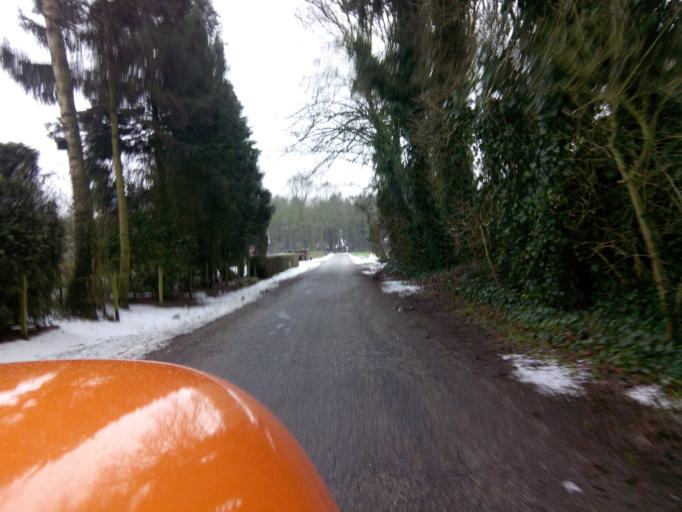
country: NL
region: Gelderland
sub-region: Gemeente Barneveld
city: Voorthuizen
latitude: 52.2206
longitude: 5.6028
